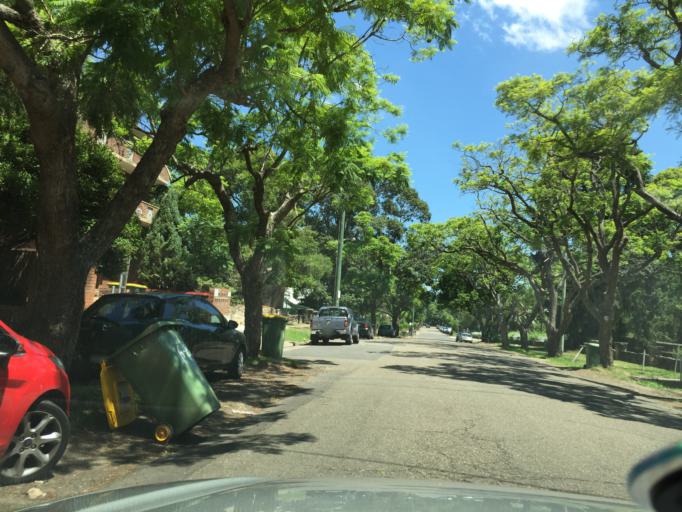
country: AU
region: New South Wales
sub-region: Parramatta
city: City of Parramatta
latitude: -33.8018
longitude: 151.0017
